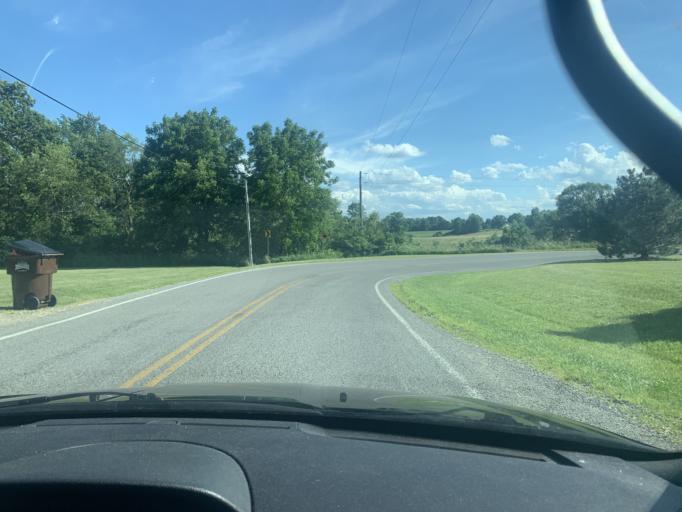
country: US
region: Ohio
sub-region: Logan County
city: Bellefontaine
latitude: 40.3435
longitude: -83.8198
